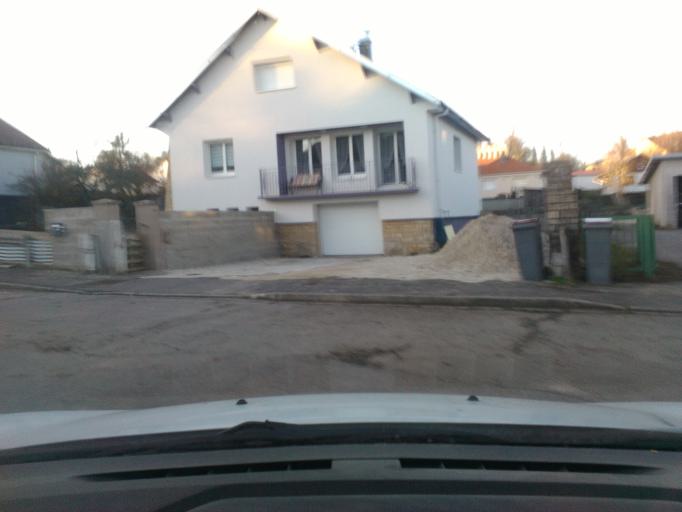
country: FR
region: Lorraine
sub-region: Departement des Vosges
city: Mirecourt
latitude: 48.2964
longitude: 6.1268
